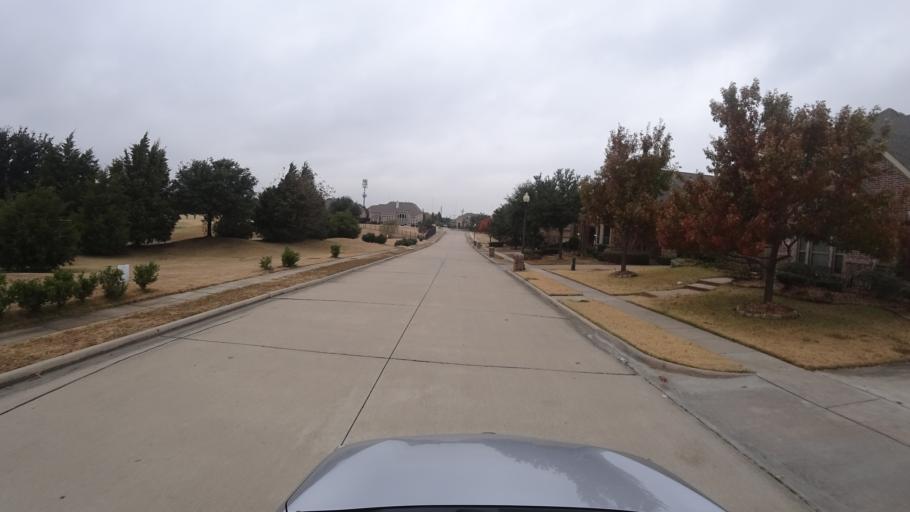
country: US
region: Texas
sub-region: Denton County
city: Lewisville
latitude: 33.0384
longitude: -96.9334
